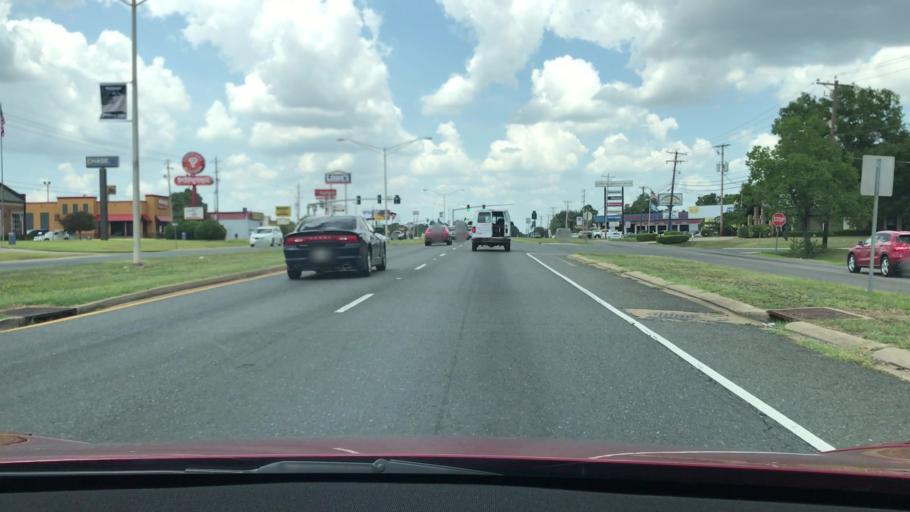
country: US
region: Louisiana
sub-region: De Soto Parish
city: Stonewall
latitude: 32.4059
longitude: -93.8004
